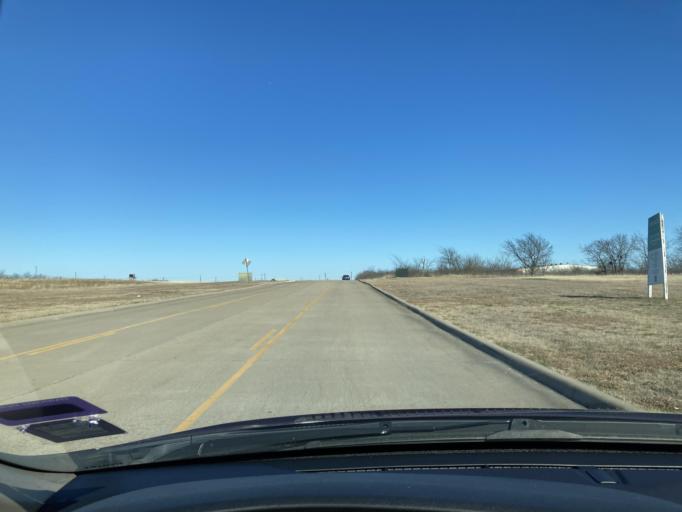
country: US
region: Texas
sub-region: Navarro County
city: Corsicana
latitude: 32.0628
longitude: -96.4440
